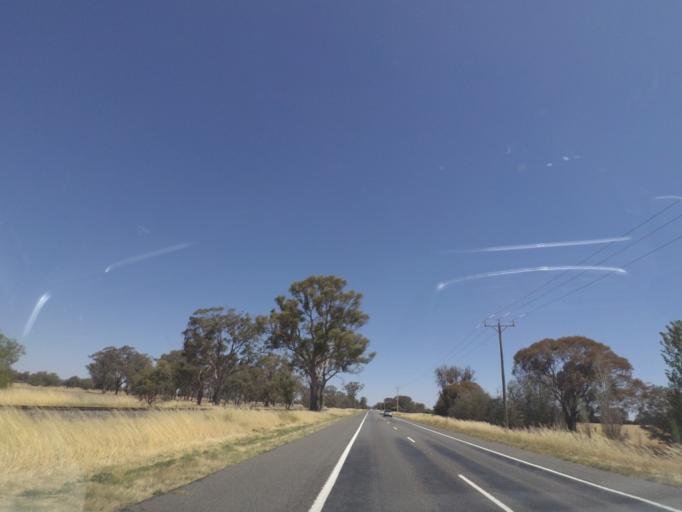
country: AU
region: Victoria
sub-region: Greater Shepparton
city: Shepparton
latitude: -36.2090
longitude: 145.4319
